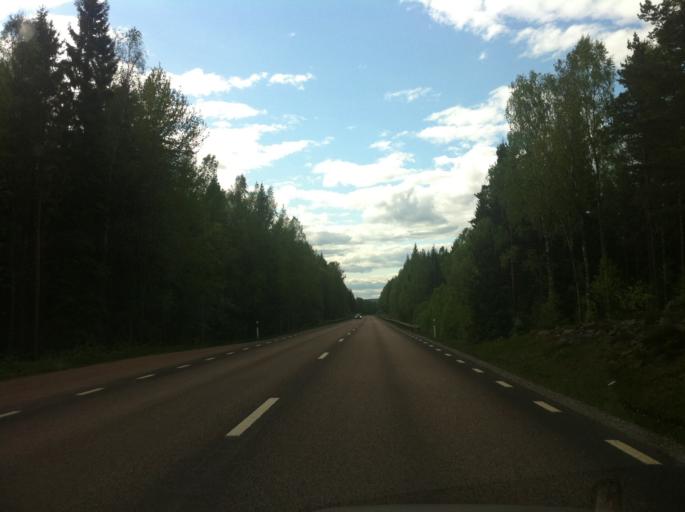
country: SE
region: Vaermland
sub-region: Filipstads Kommun
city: Filipstad
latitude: 59.6505
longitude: 14.2388
